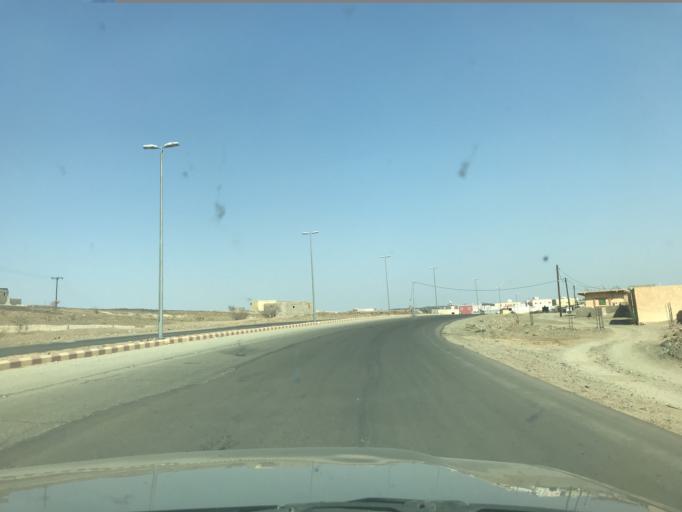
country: SA
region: Mintaqat al Bahah
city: Al Bahah
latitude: 20.4404
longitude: 41.9237
